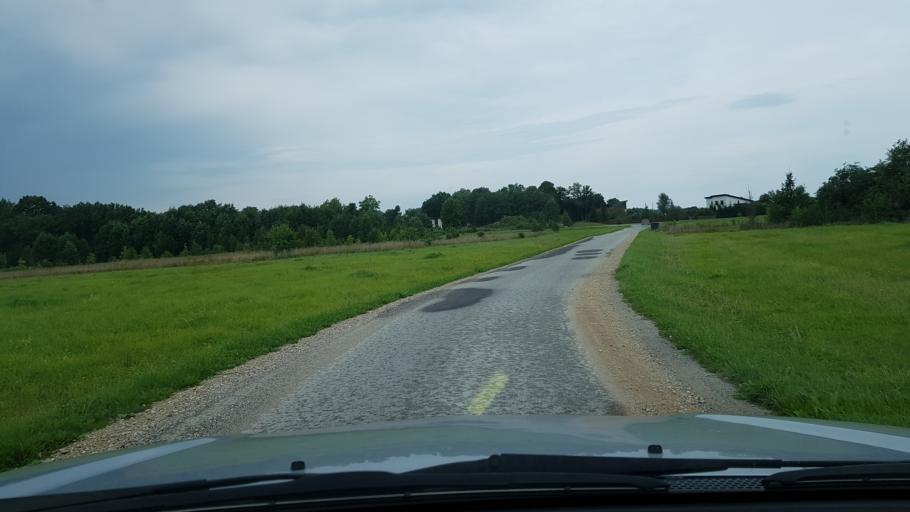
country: EE
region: Harju
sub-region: Rae vald
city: Jueri
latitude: 59.3715
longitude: 24.9277
